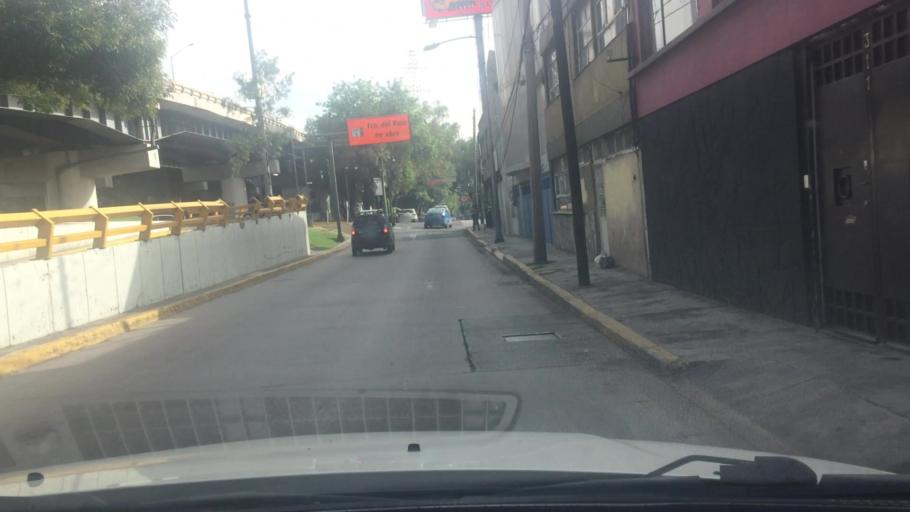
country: MX
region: Mexico City
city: Colonia Nativitas
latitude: 19.3580
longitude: -99.1313
